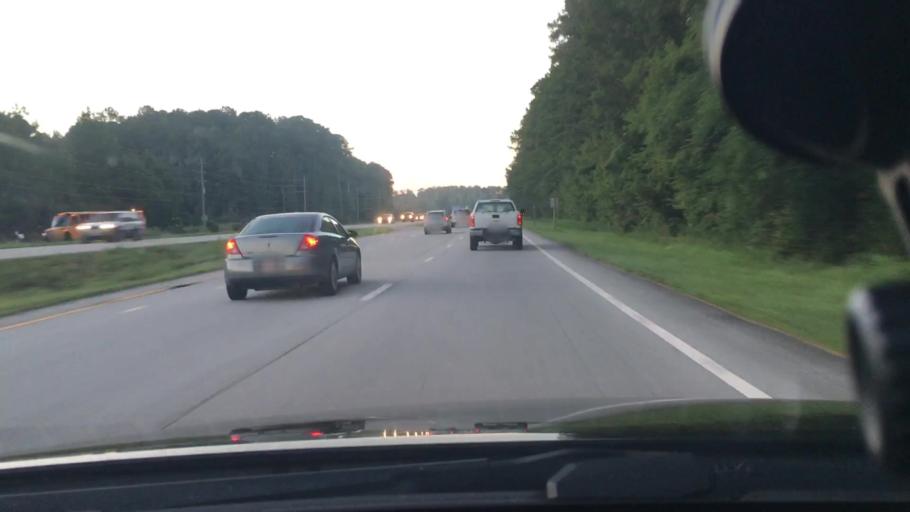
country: US
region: North Carolina
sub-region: Craven County
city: Neuse Forest
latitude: 34.9776
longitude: -76.9760
